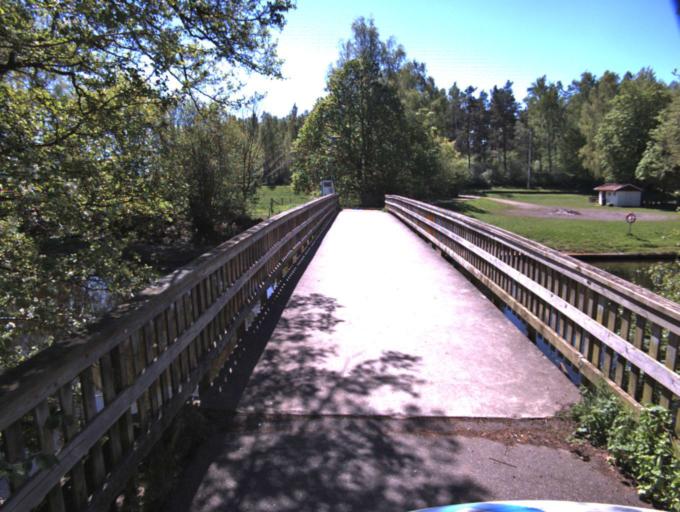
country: SE
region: Skane
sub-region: Kristianstads Kommun
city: Norra Asum
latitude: 55.9426
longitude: 14.1570
